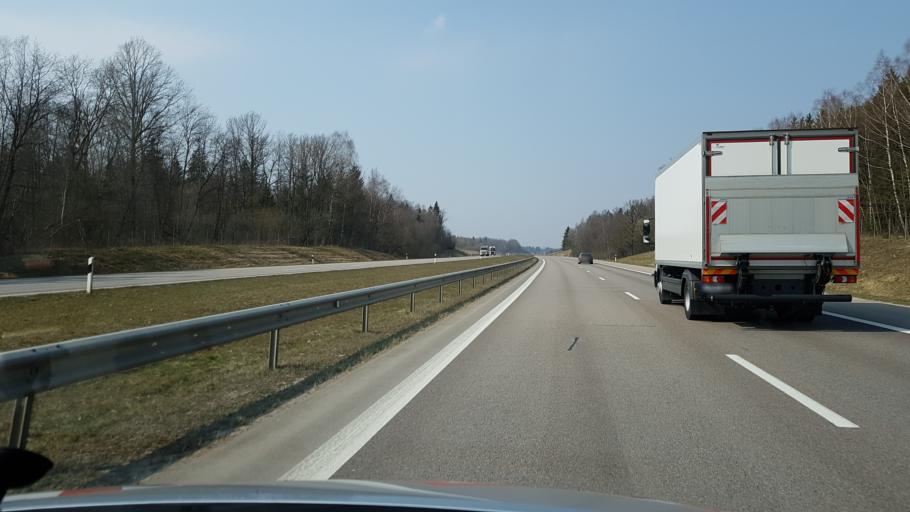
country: LT
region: Vilnius County
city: Pasilaiciai
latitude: 54.8478
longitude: 25.1059
